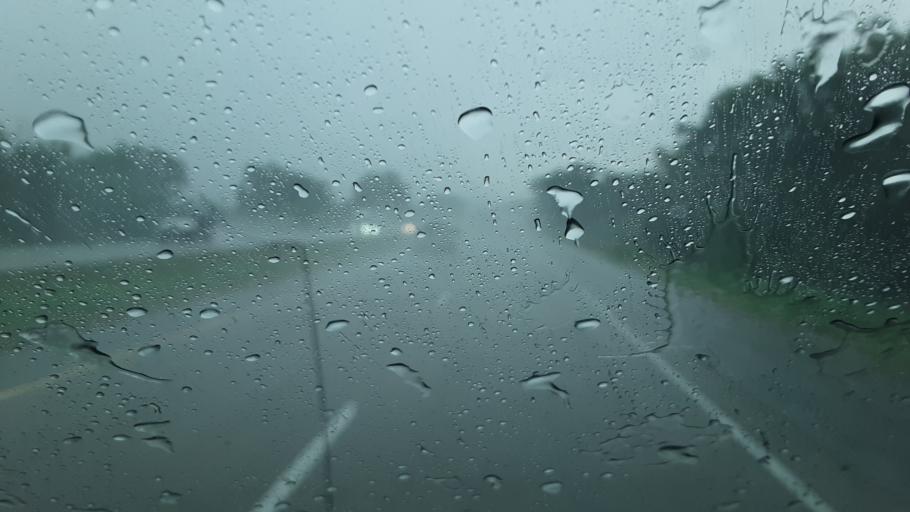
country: US
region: Iowa
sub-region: Pottawattamie County
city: Council Bluffs
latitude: 41.2555
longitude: -95.8073
